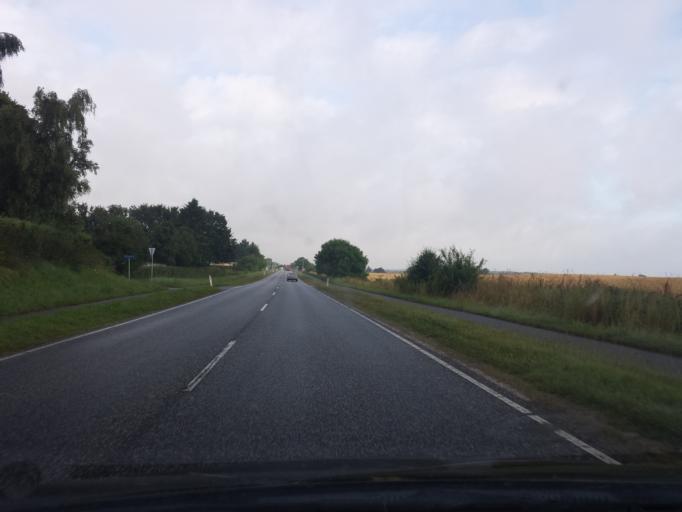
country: DK
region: South Denmark
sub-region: Sonderborg Kommune
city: Guderup
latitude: 55.0222
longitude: 9.8416
